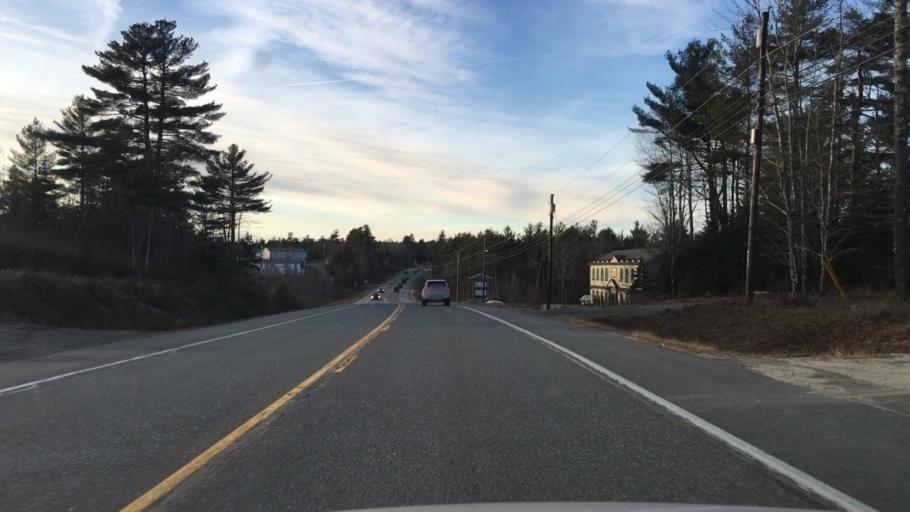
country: US
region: Maine
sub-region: Hancock County
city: Ellsworth
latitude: 44.5821
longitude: -68.4831
